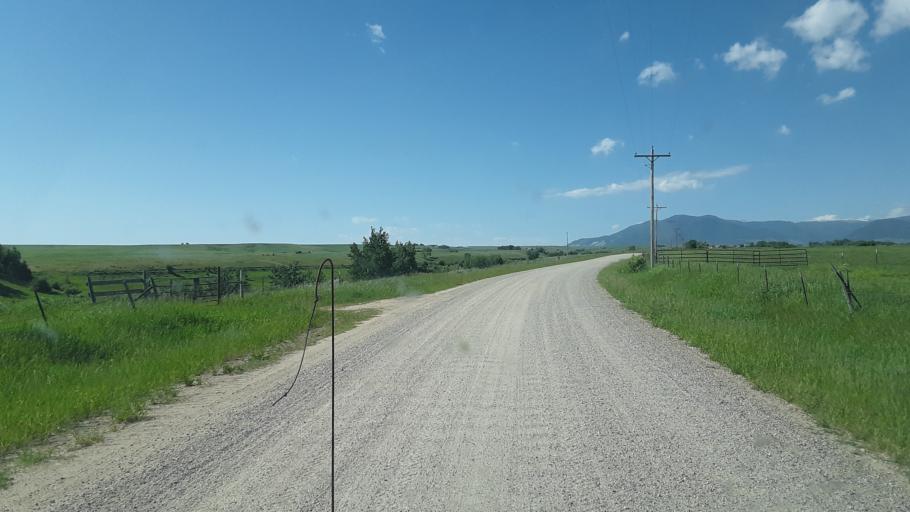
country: US
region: Montana
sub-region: Carbon County
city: Red Lodge
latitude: 45.2856
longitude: -109.1893
